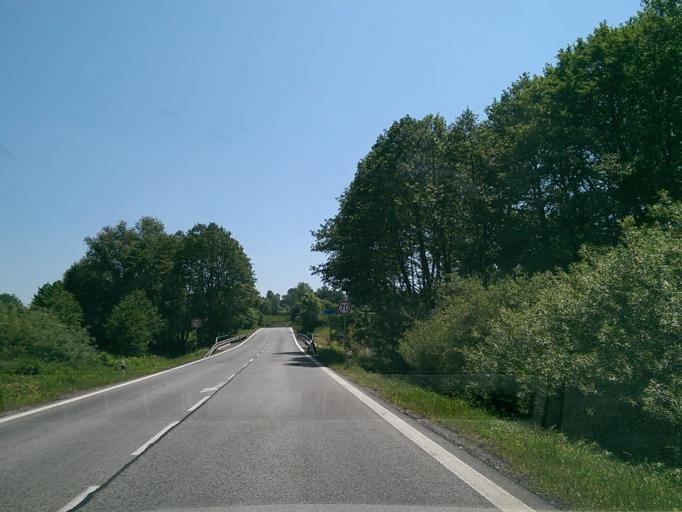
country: CZ
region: Liberecky
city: Rovensko pod Troskami
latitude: 50.4946
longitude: 15.3121
